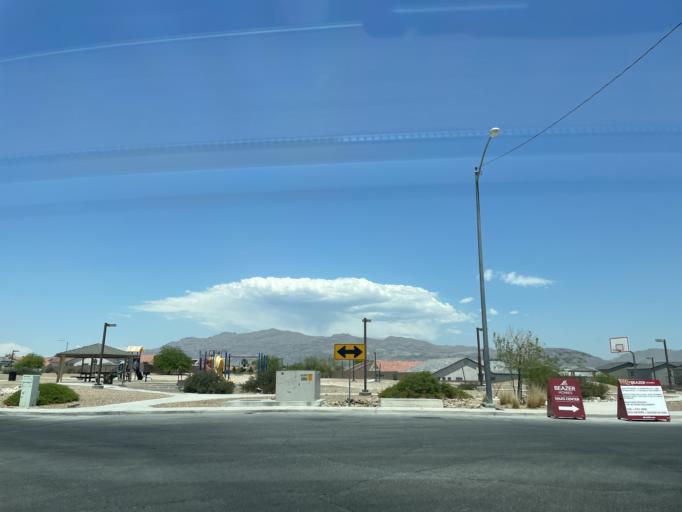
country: US
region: Nevada
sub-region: Clark County
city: North Las Vegas
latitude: 36.2628
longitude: -115.1491
